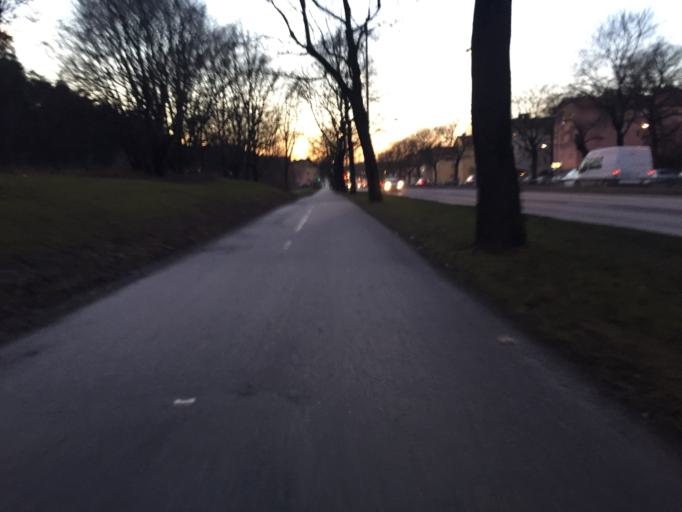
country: SE
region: Stockholm
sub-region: Stockholms Kommun
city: Bromma
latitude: 59.3361
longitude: 17.9591
